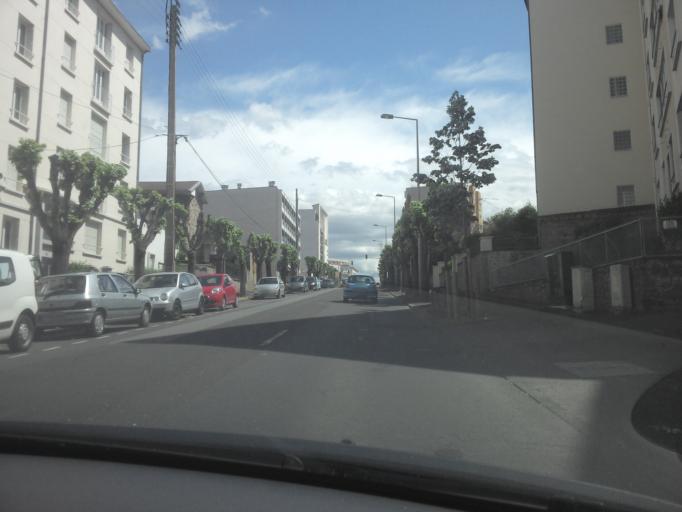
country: FR
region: Auvergne
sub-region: Departement du Puy-de-Dome
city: Clermont-Ferrand
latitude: 45.7694
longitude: 3.1030
